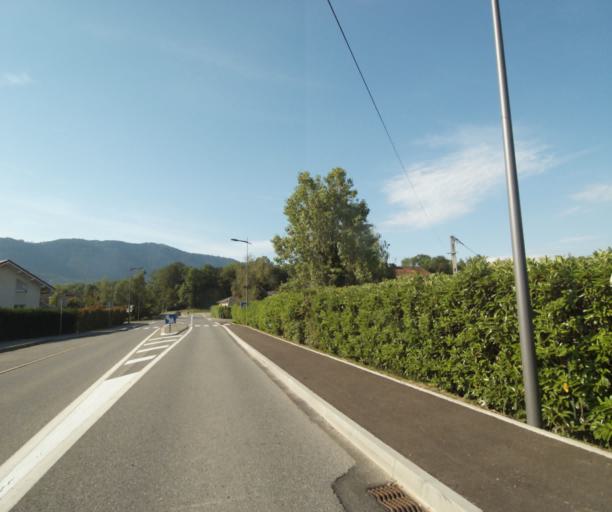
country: FR
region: Rhone-Alpes
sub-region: Departement de la Haute-Savoie
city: Armoy
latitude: 46.3536
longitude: 6.5149
